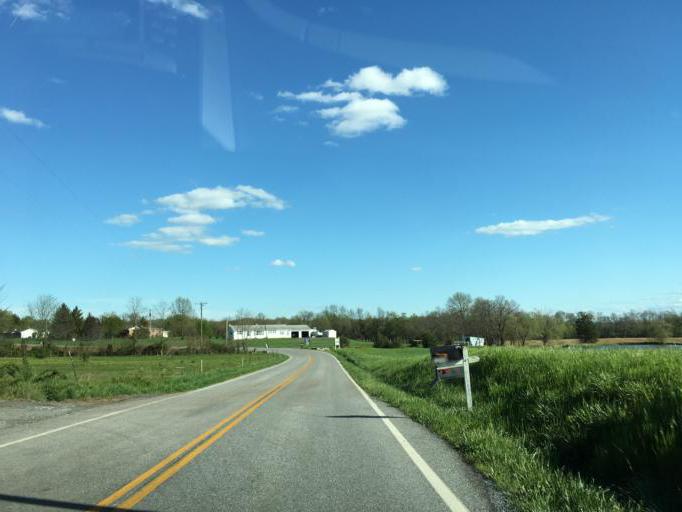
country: US
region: Maryland
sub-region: Frederick County
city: Emmitsburg
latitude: 39.6677
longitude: -77.2948
